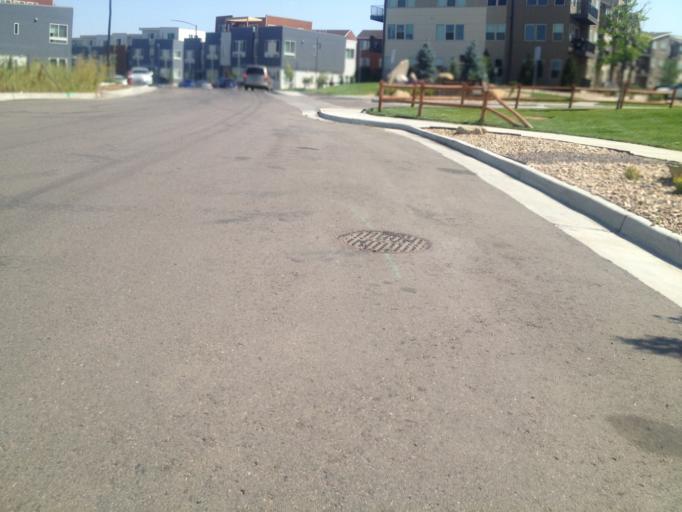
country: US
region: Colorado
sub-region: Boulder County
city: Louisville
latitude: 39.9904
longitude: -105.1312
